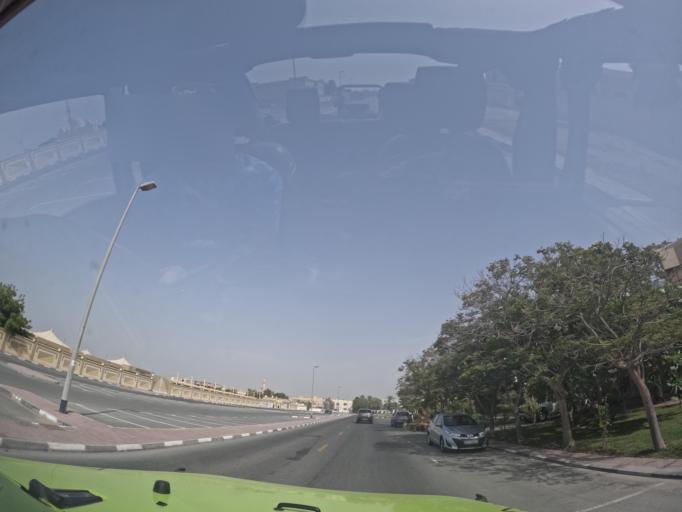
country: AE
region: Dubai
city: Dubai
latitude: 25.1460
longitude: 55.2152
